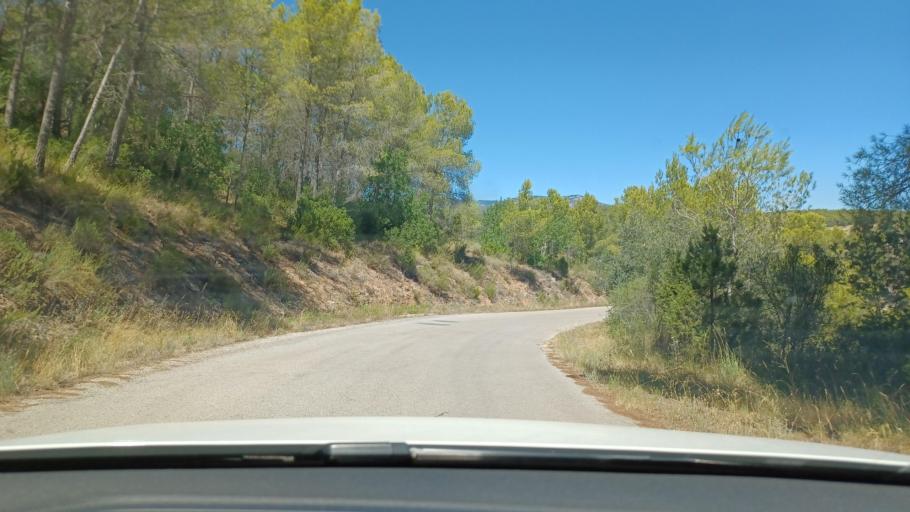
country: ES
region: Catalonia
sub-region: Provincia de Tarragona
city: Benifallet
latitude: 40.9527
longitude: 0.5050
